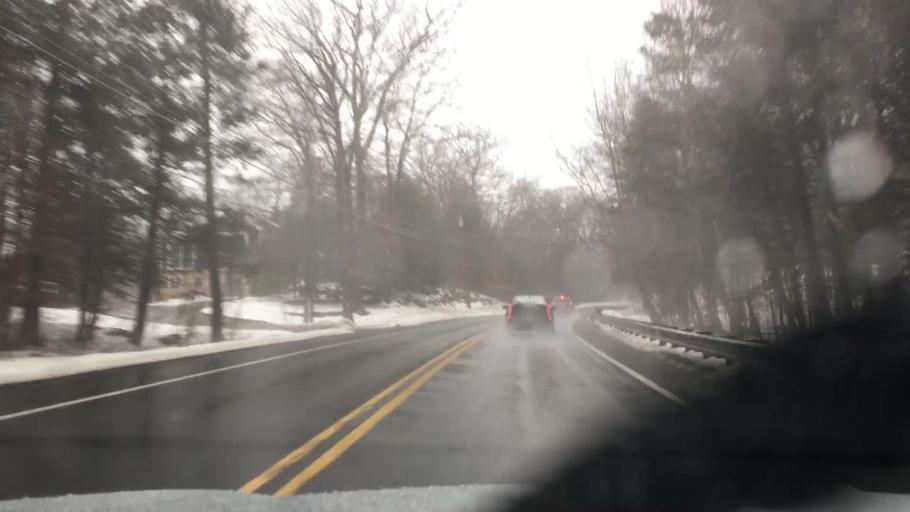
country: US
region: Massachusetts
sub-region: Franklin County
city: Wendell
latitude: 42.5013
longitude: -72.3384
